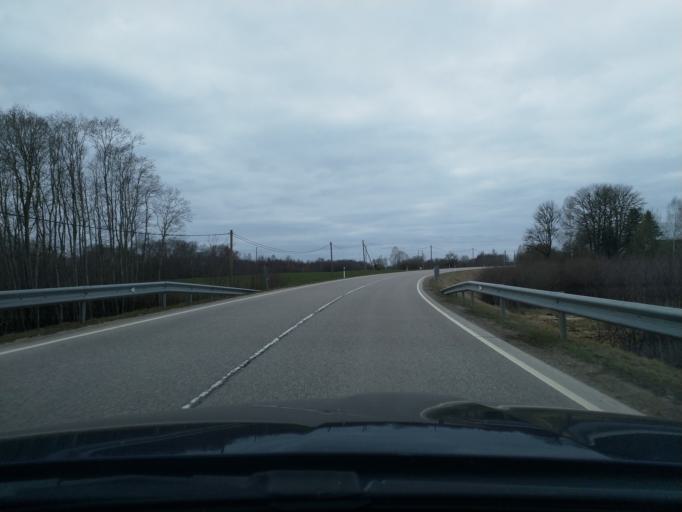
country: LV
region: Talsu Rajons
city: Sabile
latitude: 56.9304
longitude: 22.5245
